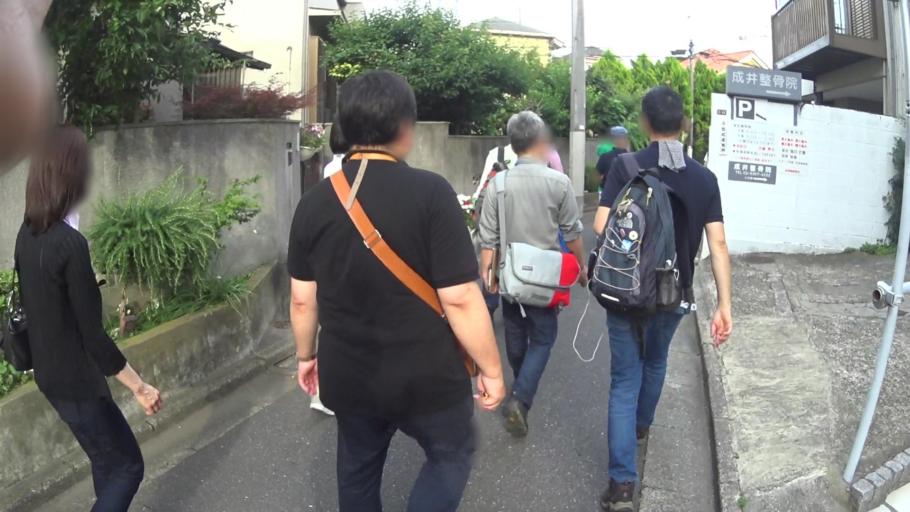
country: JP
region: Tokyo
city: Musashino
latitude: 35.7055
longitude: 139.6257
